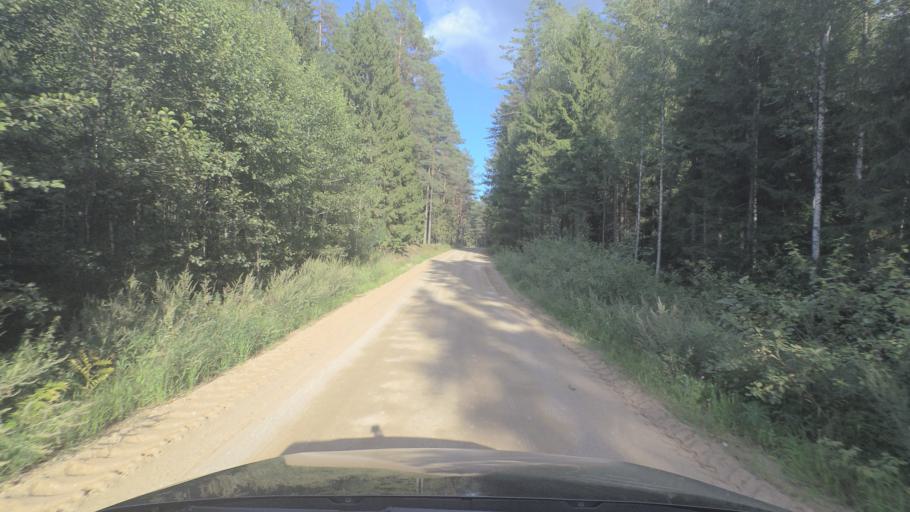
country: LT
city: Pabrade
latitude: 55.1550
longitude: 25.7903
